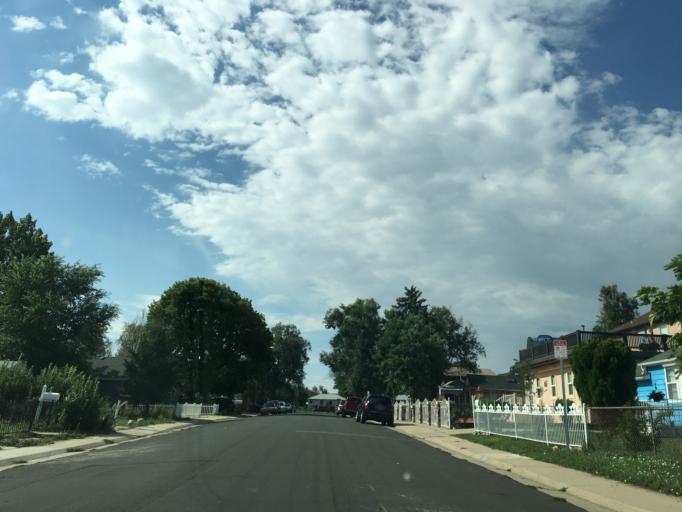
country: US
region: Colorado
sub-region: Jefferson County
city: Lakewood
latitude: 39.7056
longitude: -105.0371
